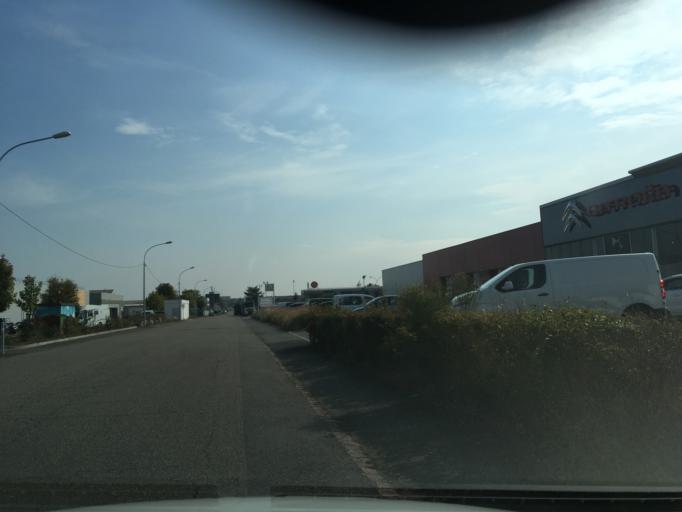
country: FR
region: Alsace
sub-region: Departement du Haut-Rhin
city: Colmar
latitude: 48.1019
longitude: 7.3630
